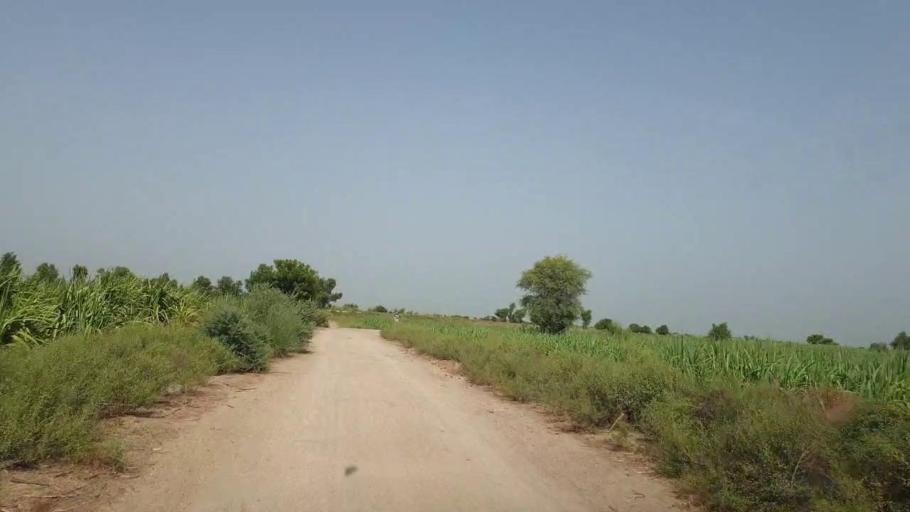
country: PK
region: Sindh
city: Sakrand
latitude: 26.3057
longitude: 68.2119
